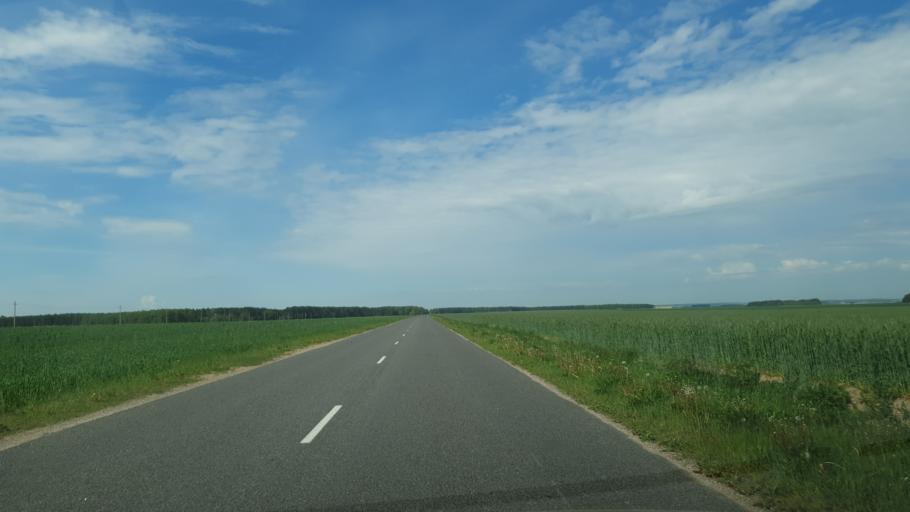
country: BY
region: Grodnenskaya
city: Mir
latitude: 53.4337
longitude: 26.4100
